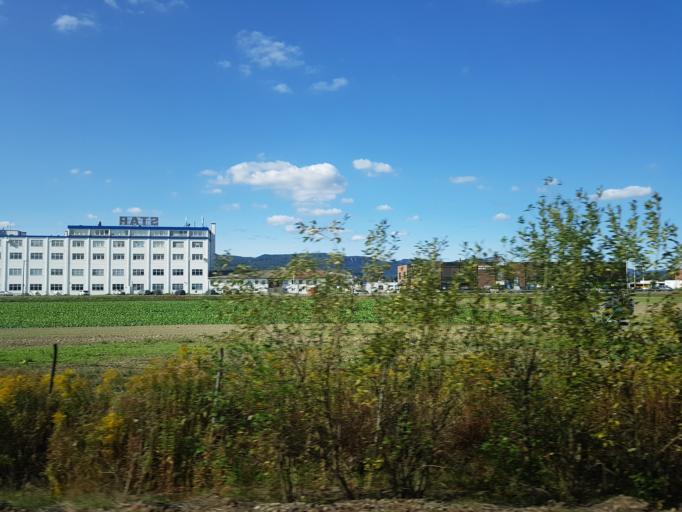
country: NO
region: Buskerud
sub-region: Lier
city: Lierbyen
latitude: 59.7558
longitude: 10.2697
